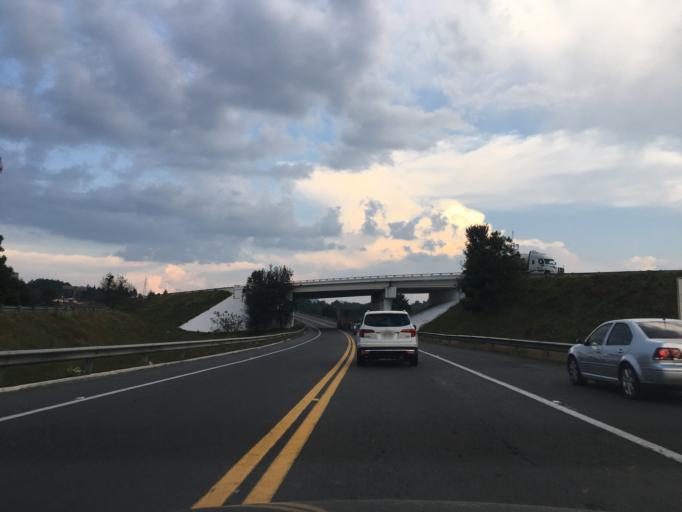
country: MX
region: Michoacan
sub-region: Patzcuaro
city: Colonia Vista Bella (Lomas del Peaje)
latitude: 19.4931
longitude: -101.6014
